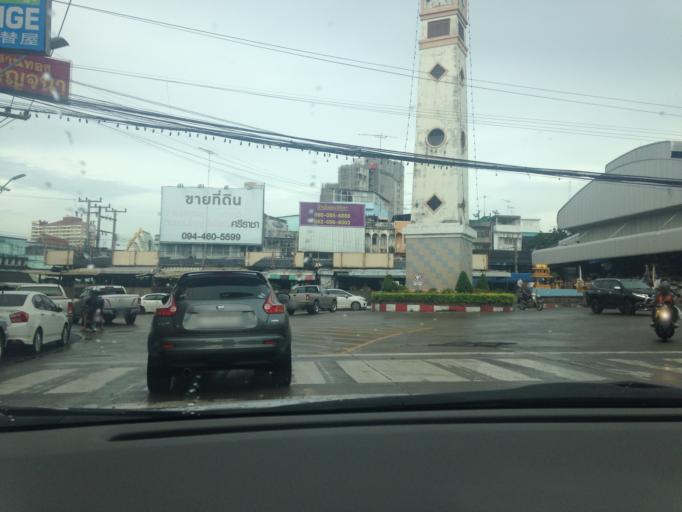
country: TH
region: Chon Buri
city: Si Racha
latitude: 13.1641
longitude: 100.9219
